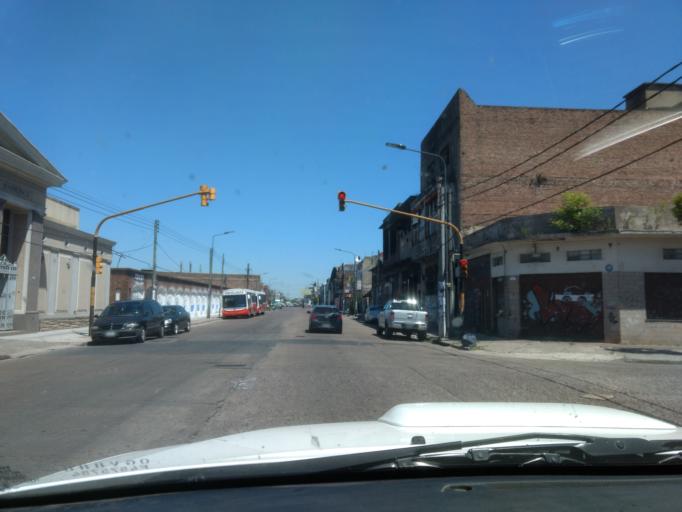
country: AR
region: Buenos Aires
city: Caseros
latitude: -34.6201
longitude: -58.5492
